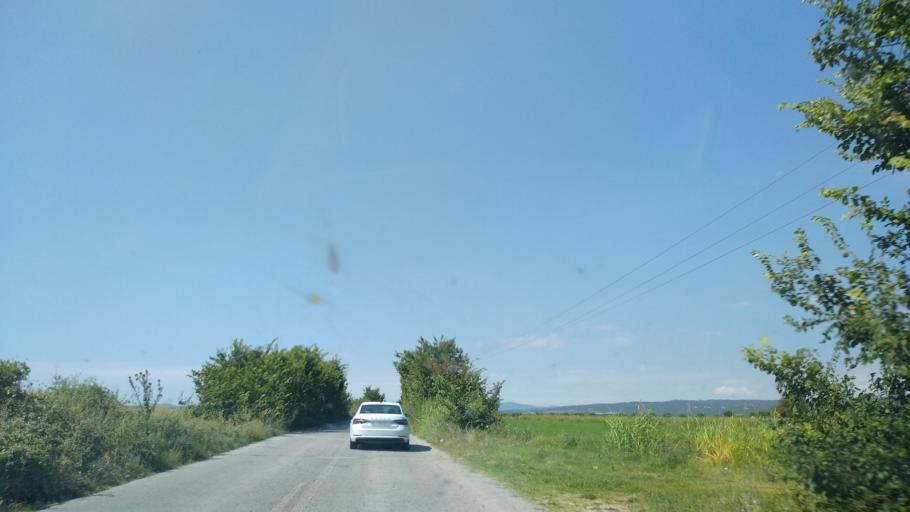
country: GR
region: Central Macedonia
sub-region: Nomos Thessalonikis
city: Nea Apollonia
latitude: 40.6331
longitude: 23.4787
